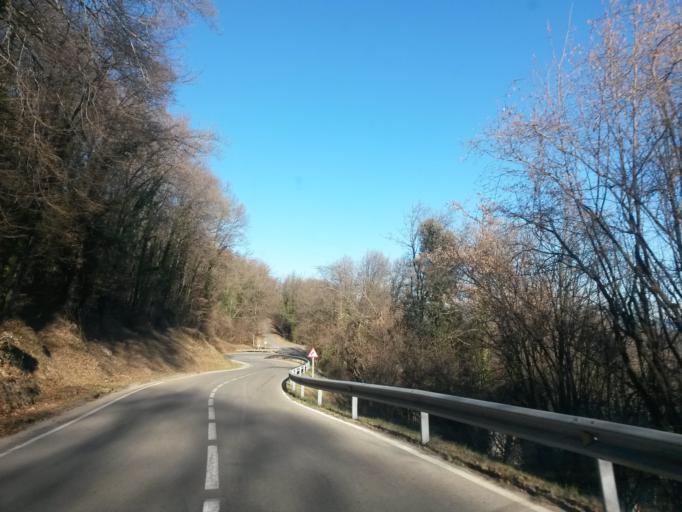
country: ES
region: Catalonia
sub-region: Provincia de Girona
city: Sant Feliu de Pallerols
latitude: 42.0569
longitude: 2.5053
